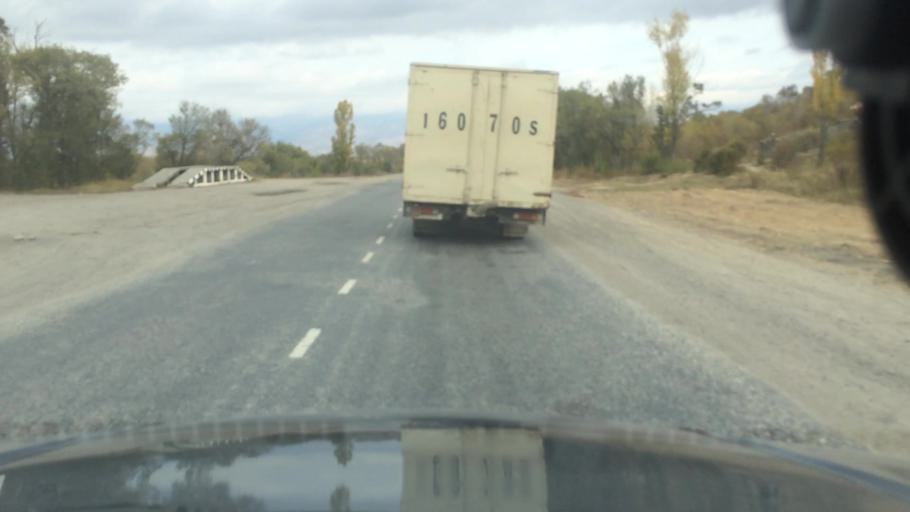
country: KG
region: Ysyk-Koel
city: Tyup
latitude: 42.6661
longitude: 78.3493
